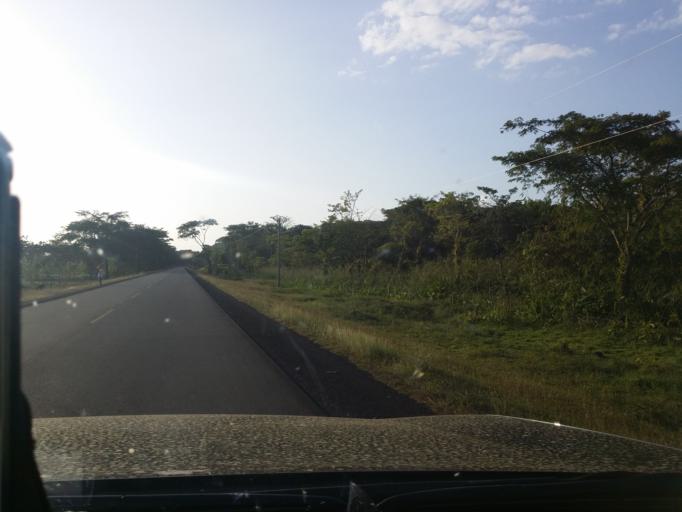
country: NI
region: Rio San Juan
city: San Miguelito
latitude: 11.3951
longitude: -84.8098
